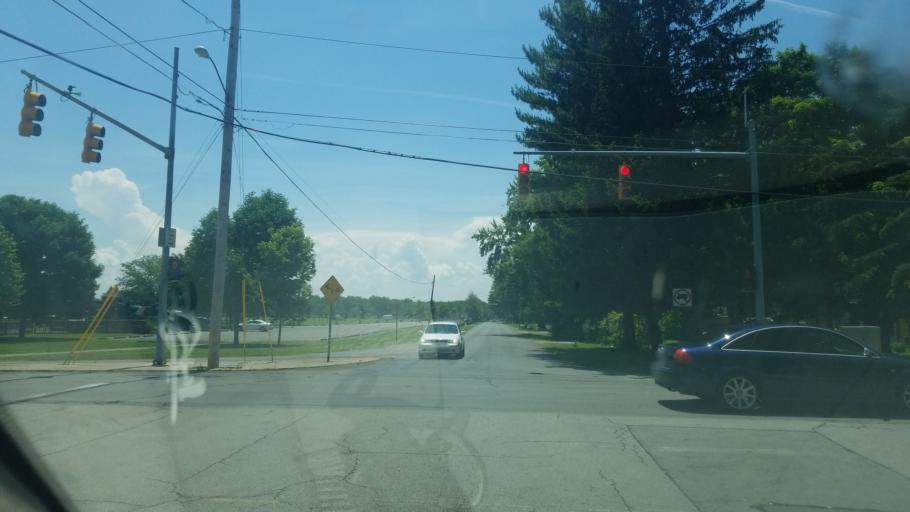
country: US
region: Ohio
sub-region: Hancock County
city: Findlay
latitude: 41.0225
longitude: -83.6412
